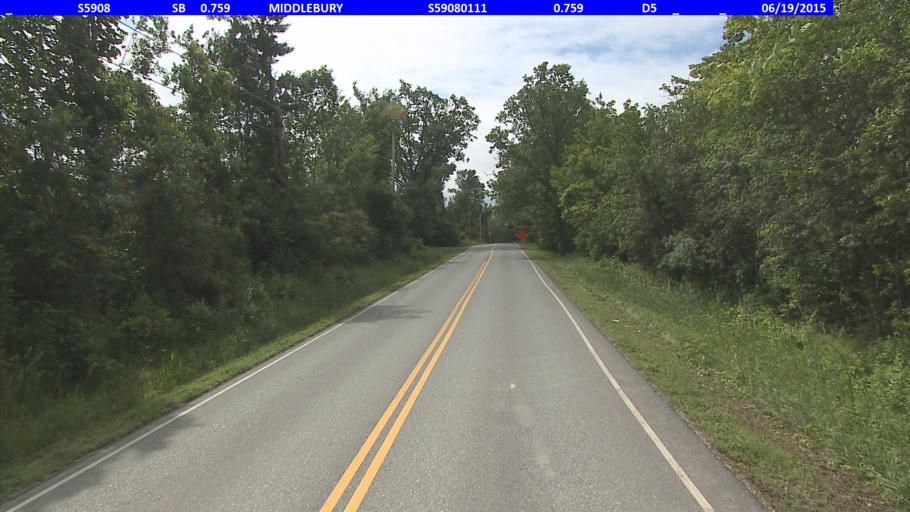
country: US
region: Vermont
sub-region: Addison County
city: Middlebury (village)
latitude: 44.0063
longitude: -73.1364
